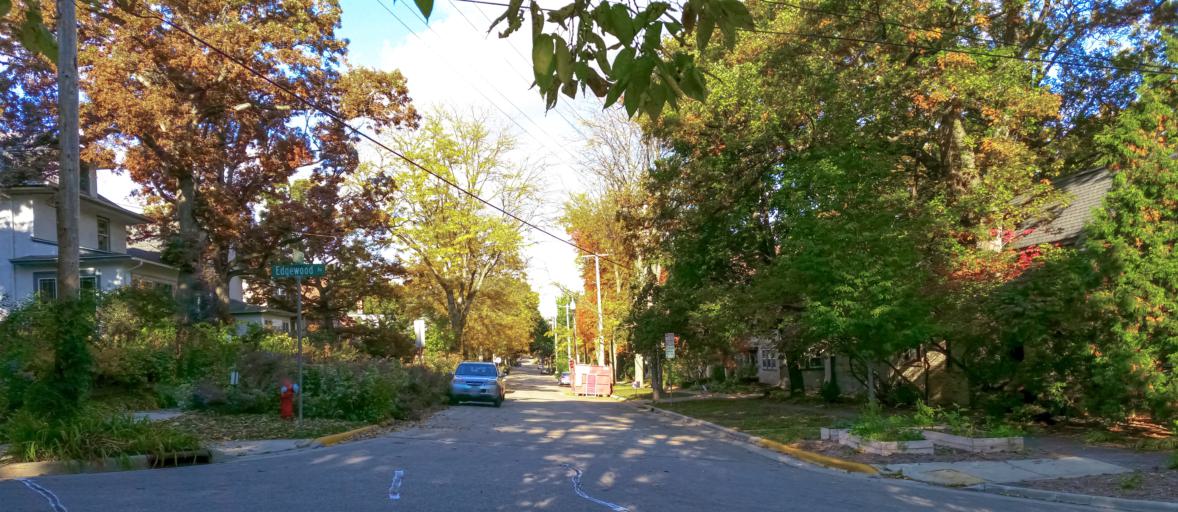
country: US
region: Wisconsin
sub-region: Dane County
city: Madison
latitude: 43.0604
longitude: -89.4188
